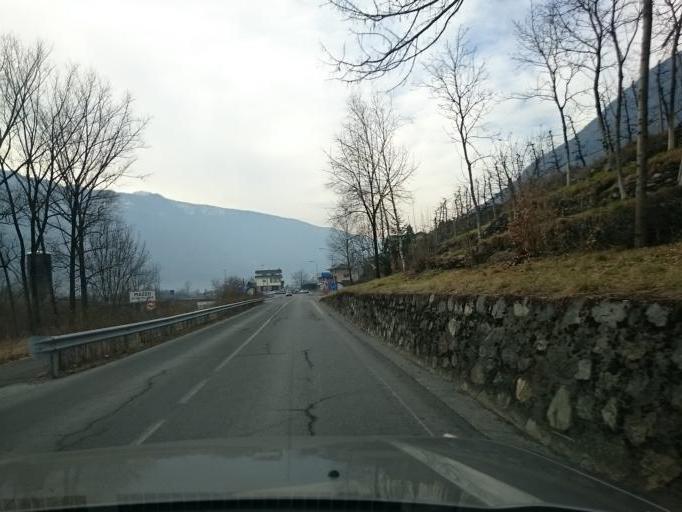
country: IT
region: Lombardy
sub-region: Provincia di Sondrio
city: Mazzo di Valtellina
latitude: 46.2631
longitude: 10.2520
